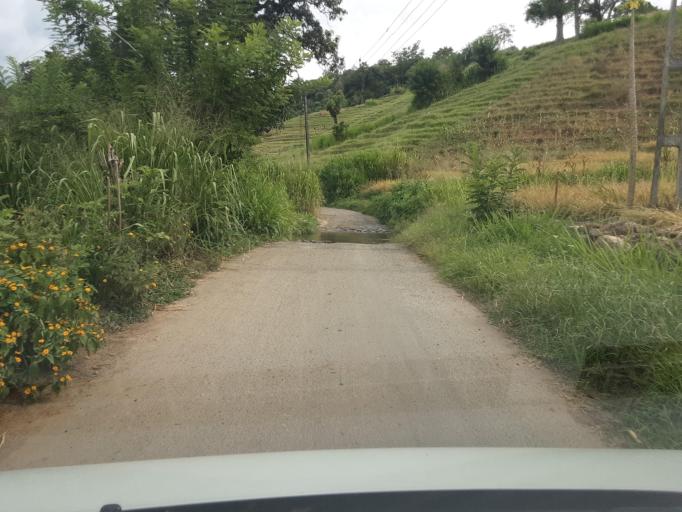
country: LK
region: Uva
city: Badulla
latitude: 7.0844
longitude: 80.9343
